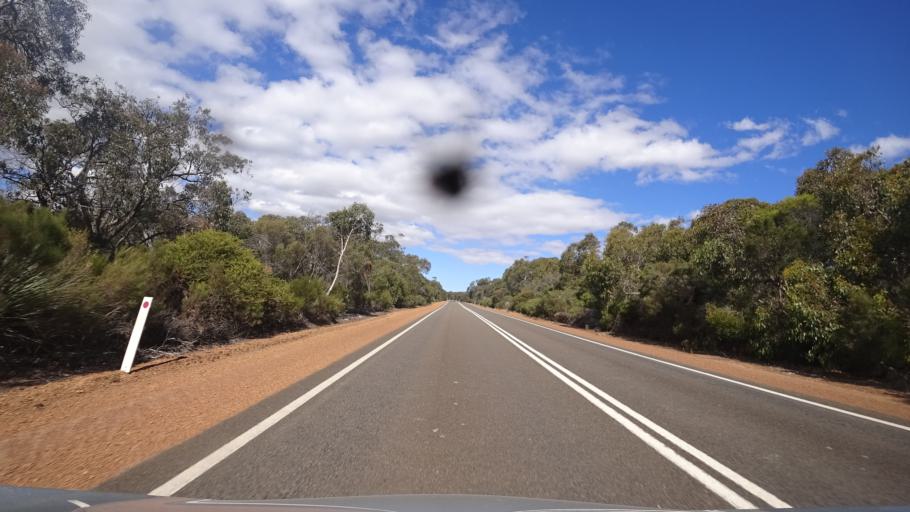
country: AU
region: South Australia
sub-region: Kangaroo Island
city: Kingscote
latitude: -35.7772
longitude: 137.3035
